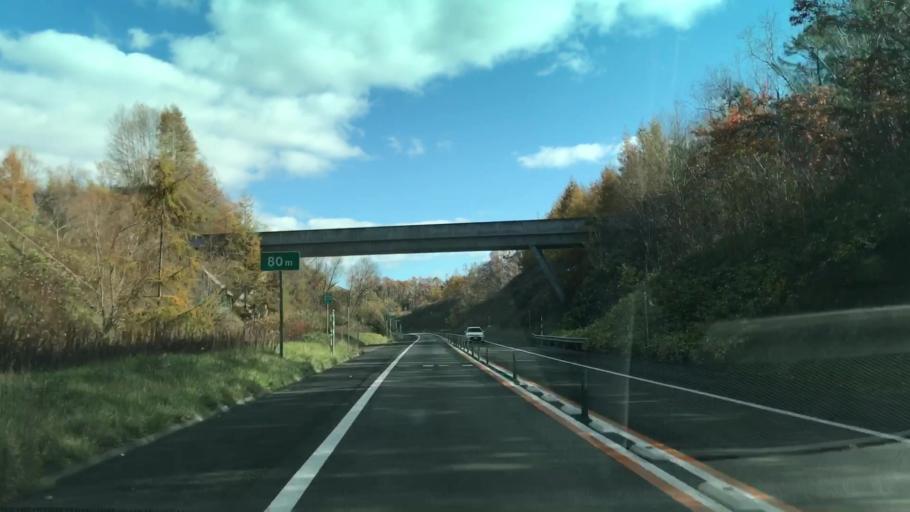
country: JP
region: Hokkaido
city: Chitose
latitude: 42.9134
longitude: 141.9251
